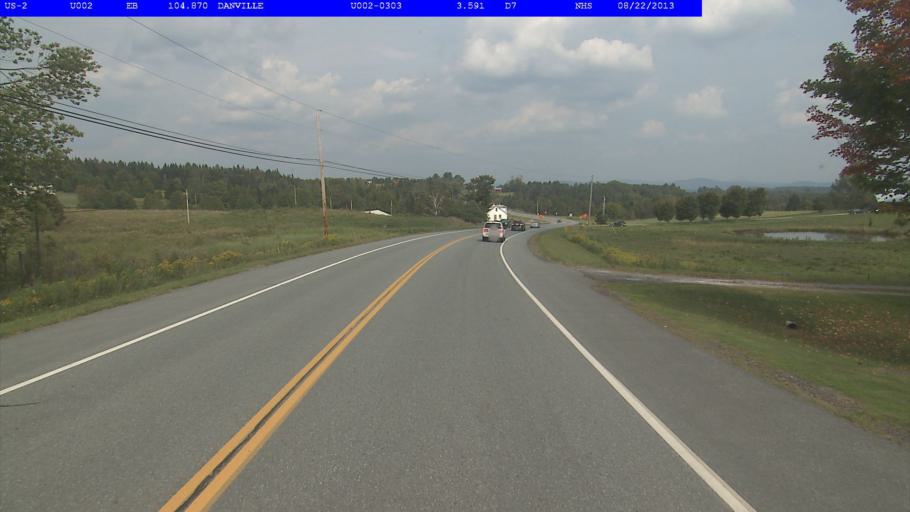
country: US
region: Vermont
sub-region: Caledonia County
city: Saint Johnsbury
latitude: 44.4099
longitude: -72.1574
